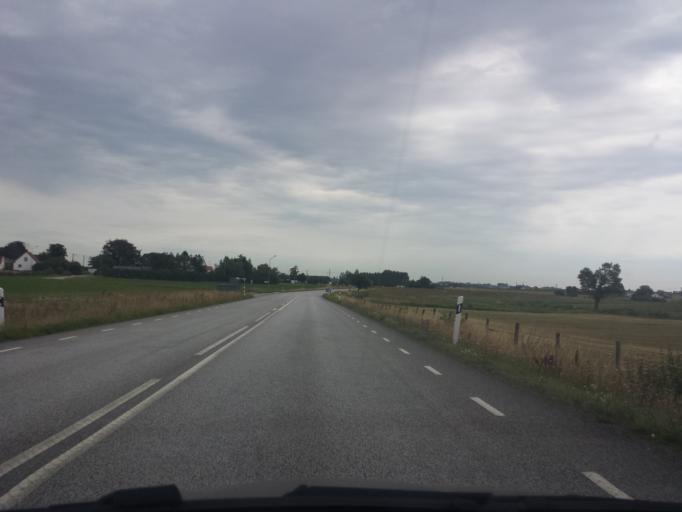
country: SE
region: Skane
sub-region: Ystads Kommun
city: Kopingebro
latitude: 55.4327
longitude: 13.9737
